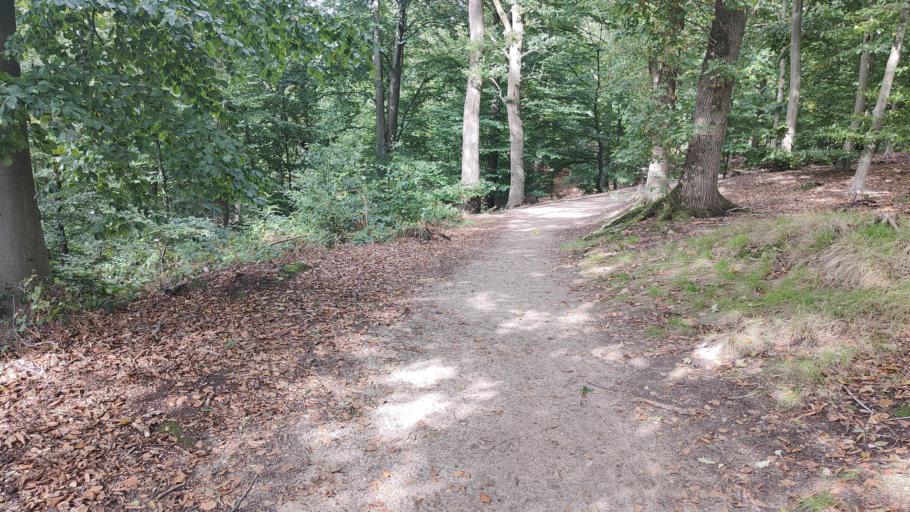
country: NL
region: Gelderland
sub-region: Gemeente Overbetuwe
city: Driel
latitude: 51.9738
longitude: 5.8184
